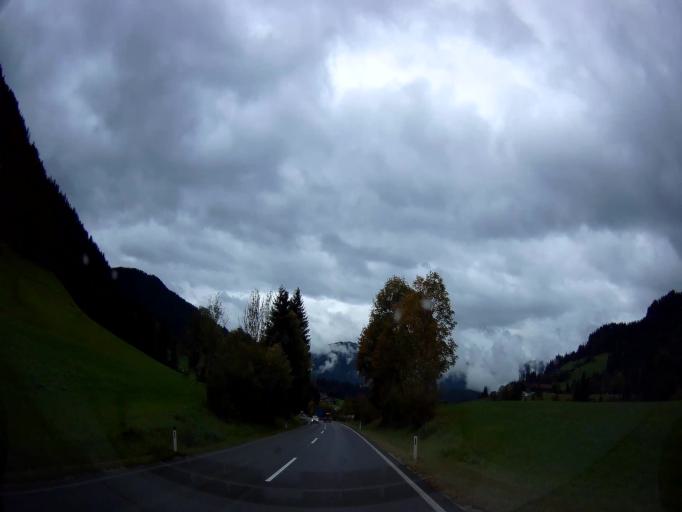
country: AT
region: Tyrol
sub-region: Politischer Bezirk Kufstein
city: Soll
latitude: 47.4920
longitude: 12.1677
